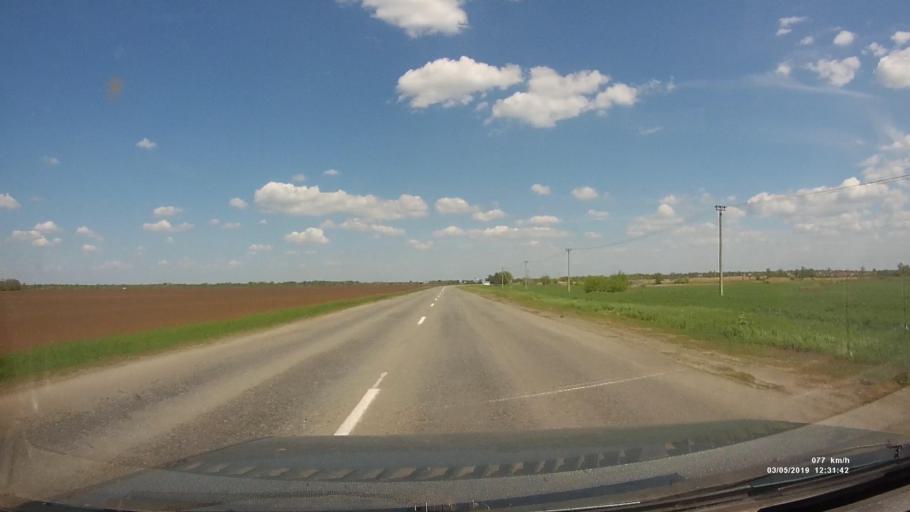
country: RU
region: Rostov
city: Semikarakorsk
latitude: 47.5064
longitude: 40.7500
